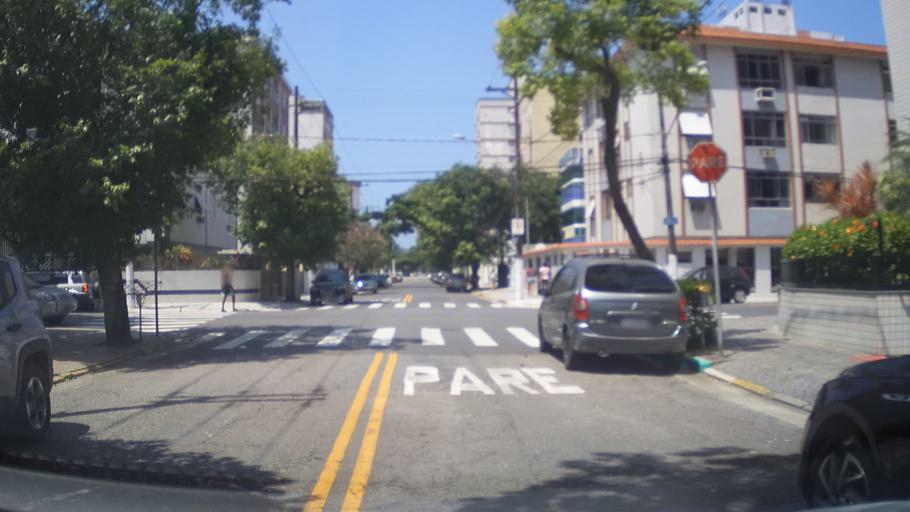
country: BR
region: Sao Paulo
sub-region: Santos
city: Santos
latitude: -23.9712
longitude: -46.3040
